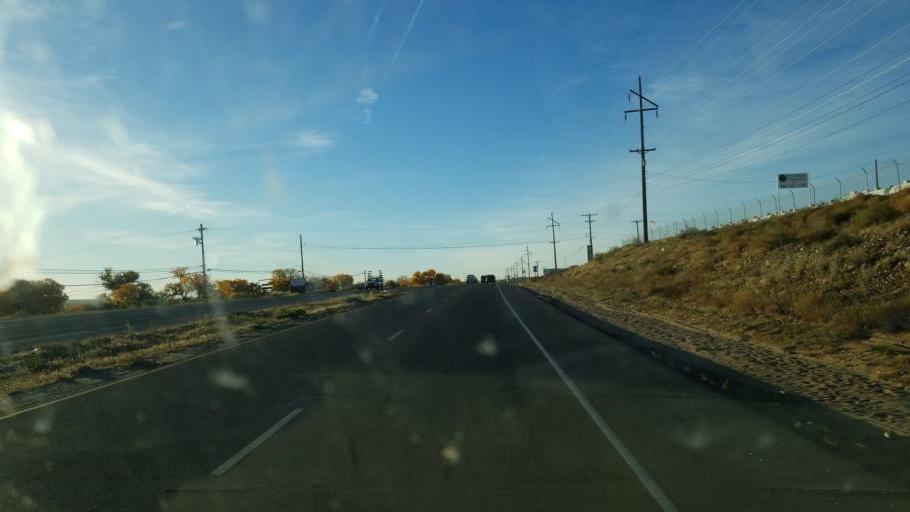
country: US
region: New Mexico
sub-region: San Juan County
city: Farmington
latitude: 36.7122
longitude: -108.1429
